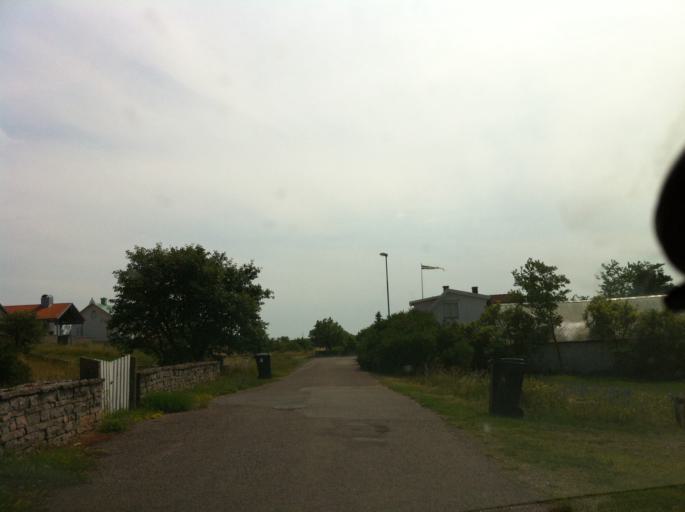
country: SE
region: Kalmar
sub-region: Borgholms Kommun
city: Borgholm
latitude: 57.0688
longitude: 16.8569
